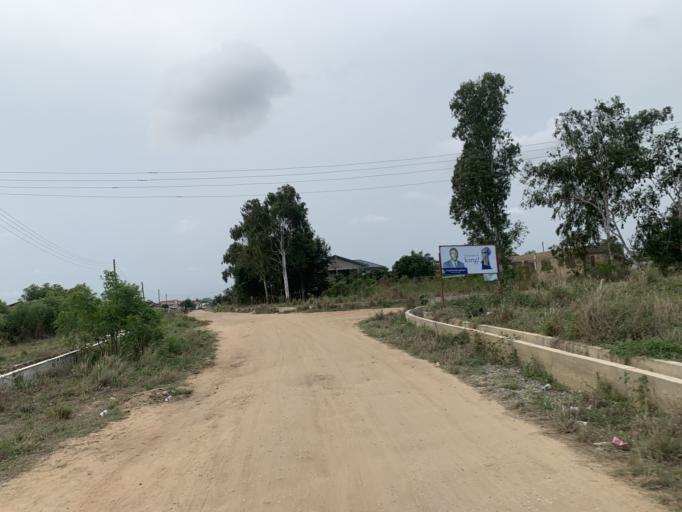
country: GH
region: Central
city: Winneba
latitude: 5.3874
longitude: -0.6337
